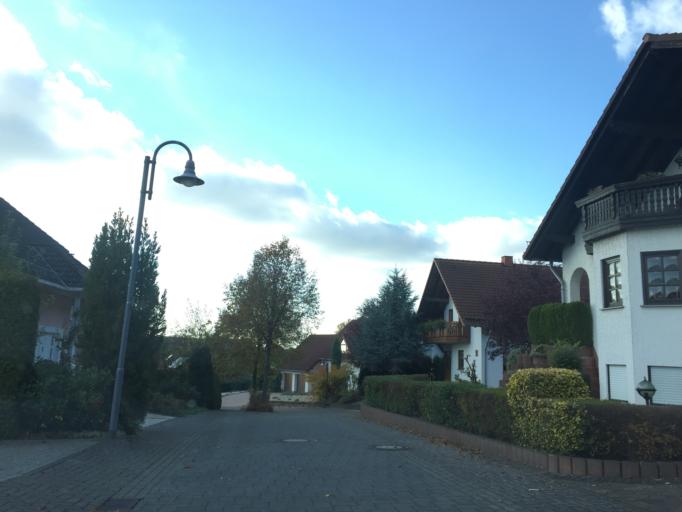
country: DE
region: Rheinland-Pfalz
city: Steinefrenz
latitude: 50.4622
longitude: 7.9365
